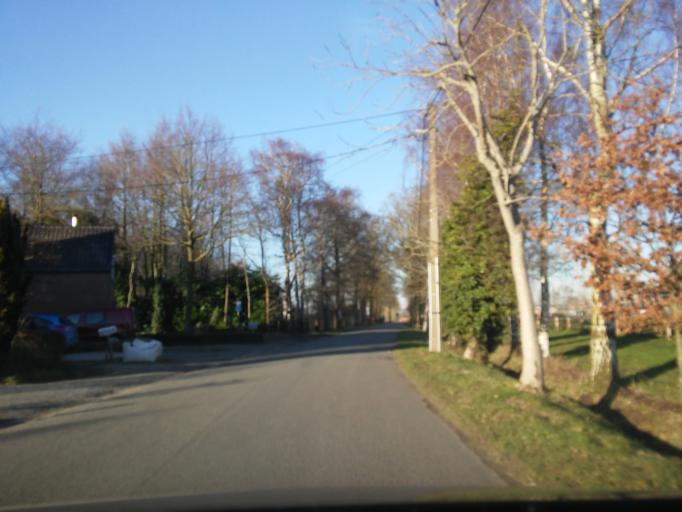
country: BE
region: Flanders
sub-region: Provincie Oost-Vlaanderen
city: Maldegem
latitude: 51.1616
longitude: 3.4749
